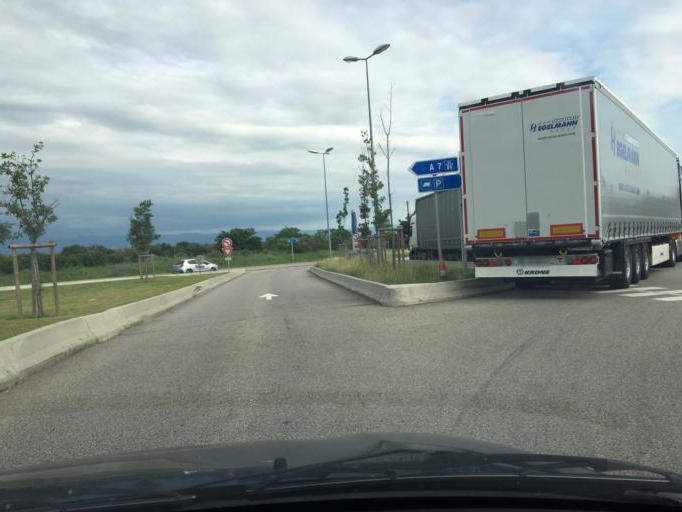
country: FR
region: Rhone-Alpes
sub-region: Departement de la Drome
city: La Roche-de-Glun
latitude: 45.0160
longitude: 4.8749
